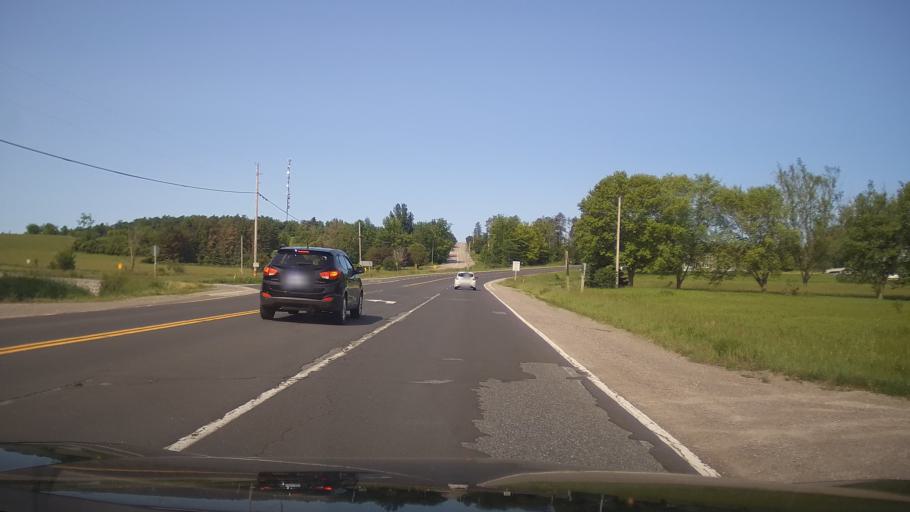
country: CA
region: Ontario
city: Omemee
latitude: 44.2929
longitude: -78.5854
